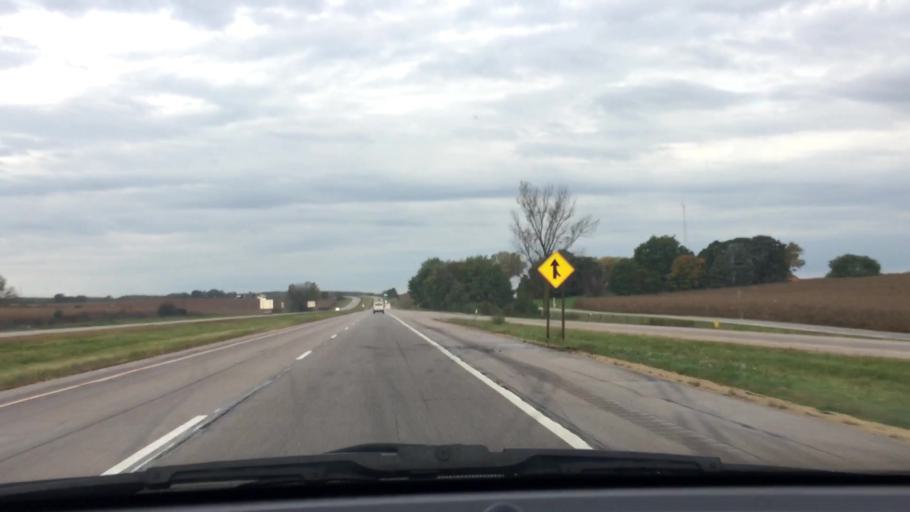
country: US
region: Wisconsin
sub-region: Rock County
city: Clinton
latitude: 42.5727
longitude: -88.8686
